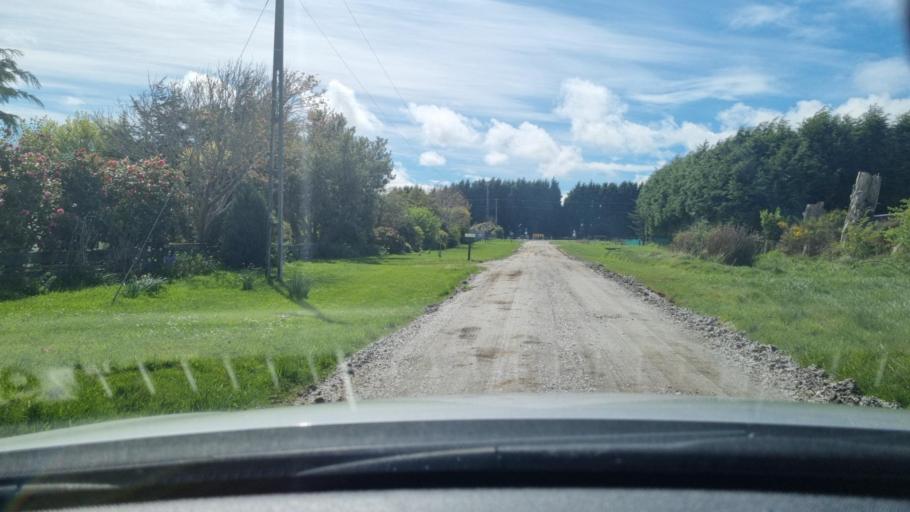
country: NZ
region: Southland
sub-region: Invercargill City
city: Invercargill
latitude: -46.4769
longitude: 168.3913
